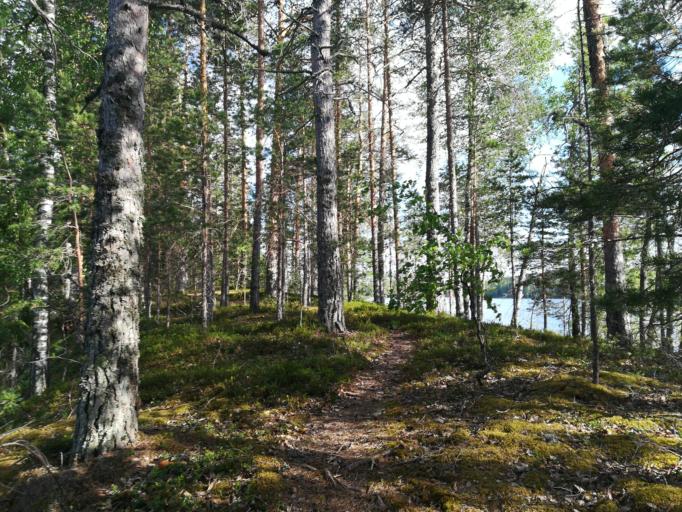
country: FI
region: Southern Savonia
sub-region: Savonlinna
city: Savonlinna
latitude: 61.6436
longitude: 28.7096
